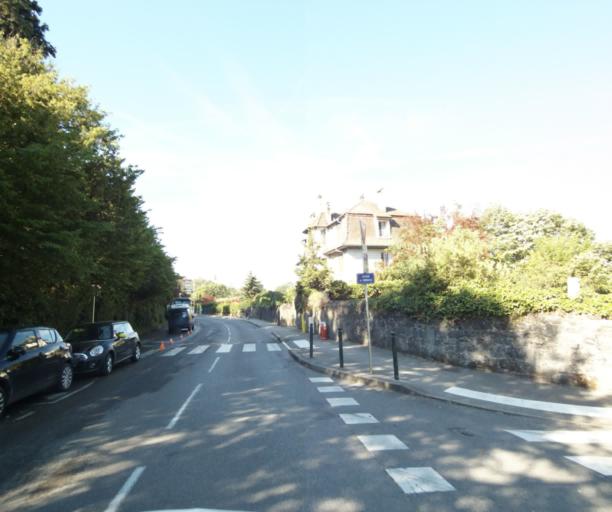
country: FR
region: Rhone-Alpes
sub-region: Departement de la Haute-Savoie
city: Thonon-les-Bains
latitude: 46.3771
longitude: 6.4828
